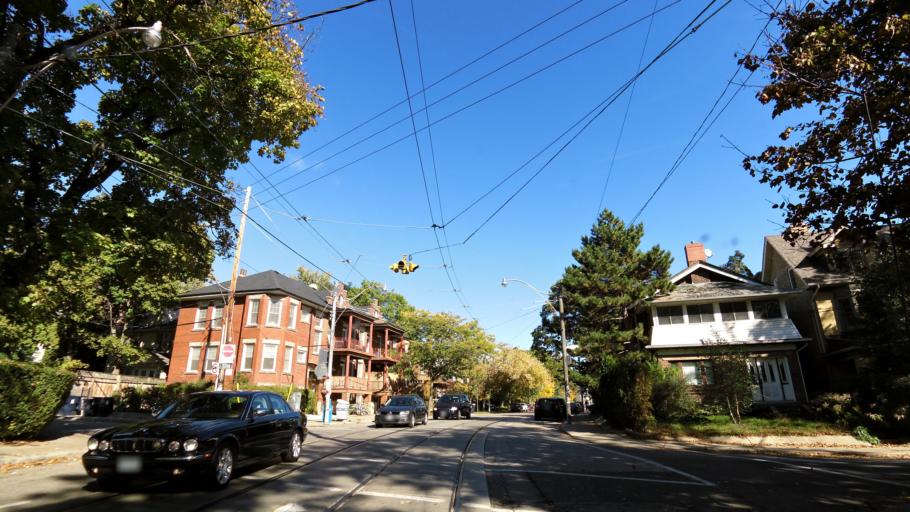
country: CA
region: Ontario
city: Toronto
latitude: 43.6506
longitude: -79.4551
